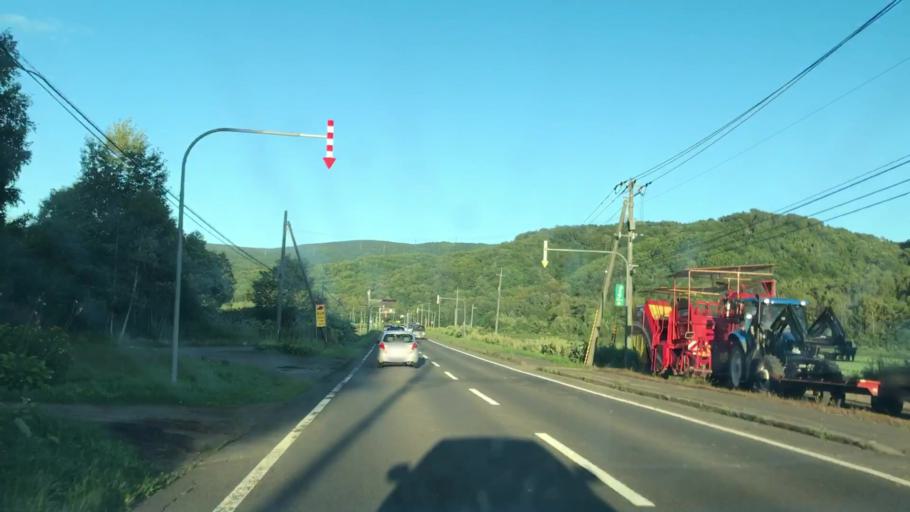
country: JP
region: Hokkaido
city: Niseko Town
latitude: 42.8003
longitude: 140.9807
